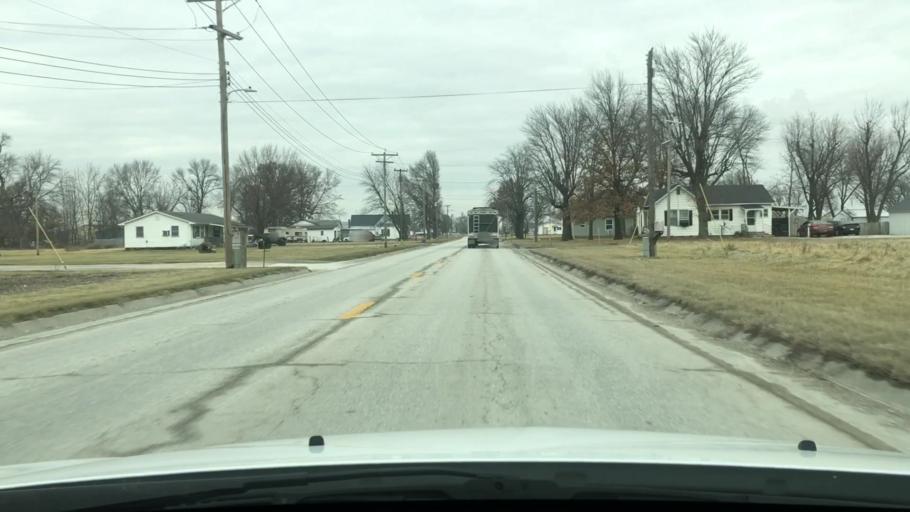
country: US
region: Missouri
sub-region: Audrain County
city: Vandalia
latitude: 39.2452
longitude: -91.6454
